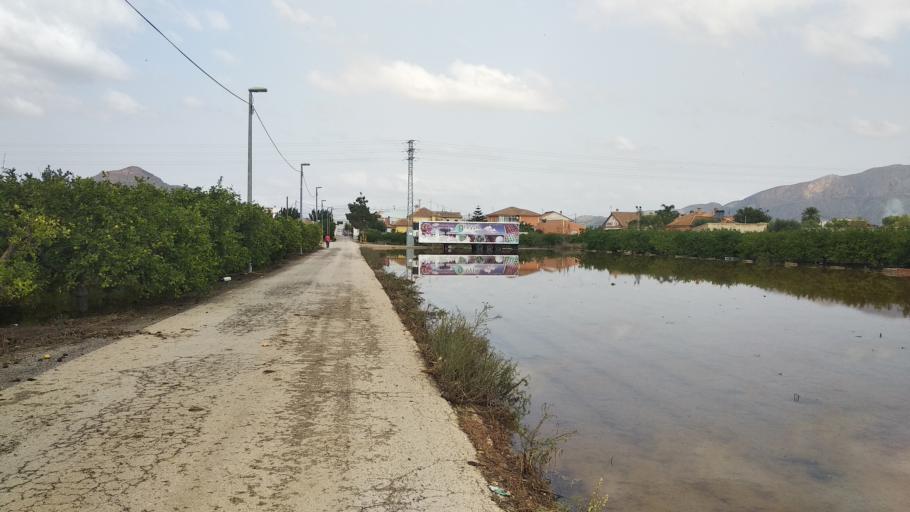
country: ES
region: Murcia
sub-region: Murcia
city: Santomera
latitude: 38.0412
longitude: -1.0408
